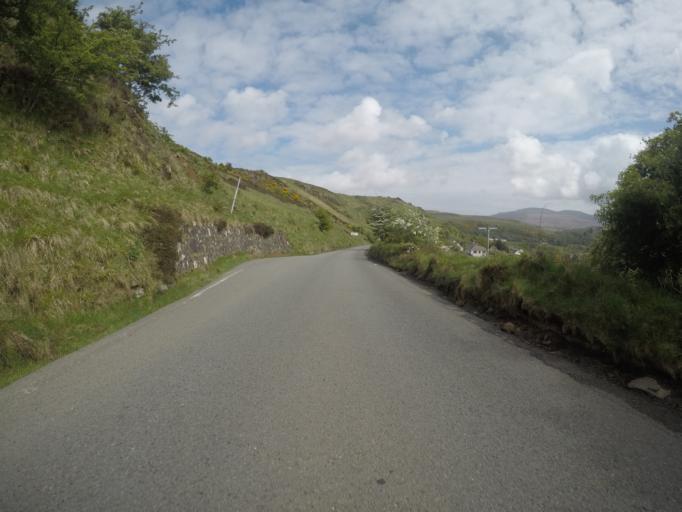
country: GB
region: Scotland
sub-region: Highland
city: Portree
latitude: 57.5920
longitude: -6.3750
